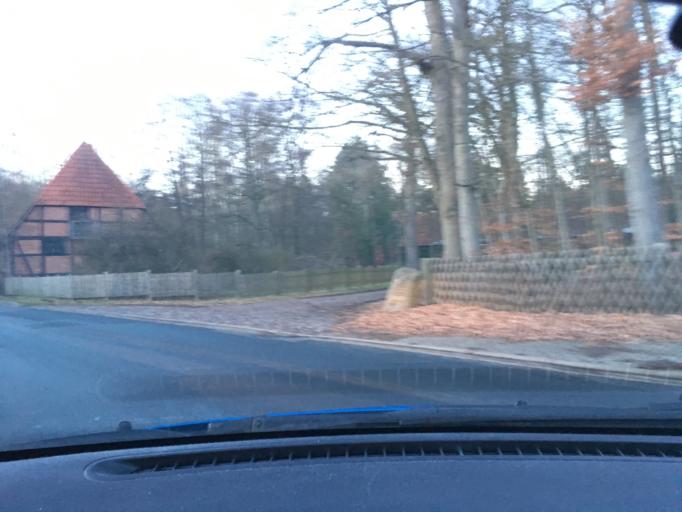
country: DE
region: Lower Saxony
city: Handeloh
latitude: 53.2654
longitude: 9.8831
